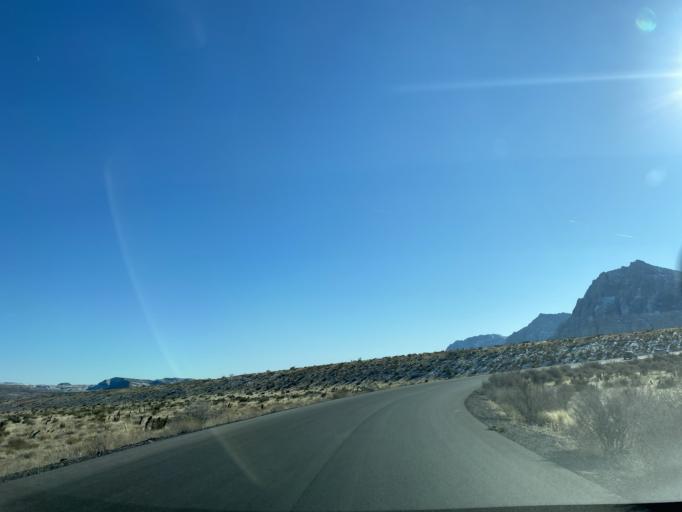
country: US
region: Nevada
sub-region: Clark County
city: Summerlin South
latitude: 36.1382
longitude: -115.4638
